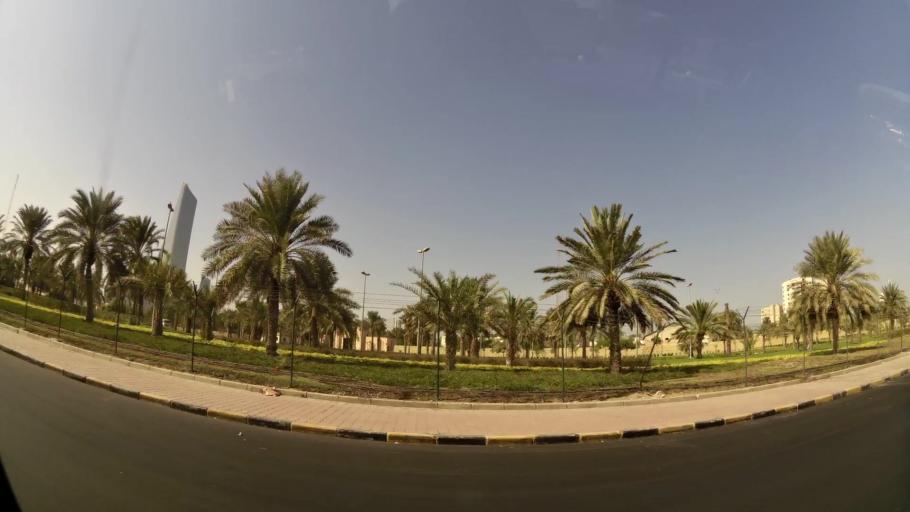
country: KW
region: Al Asimah
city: Ad Dasmah
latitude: 29.3868
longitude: 48.0021
